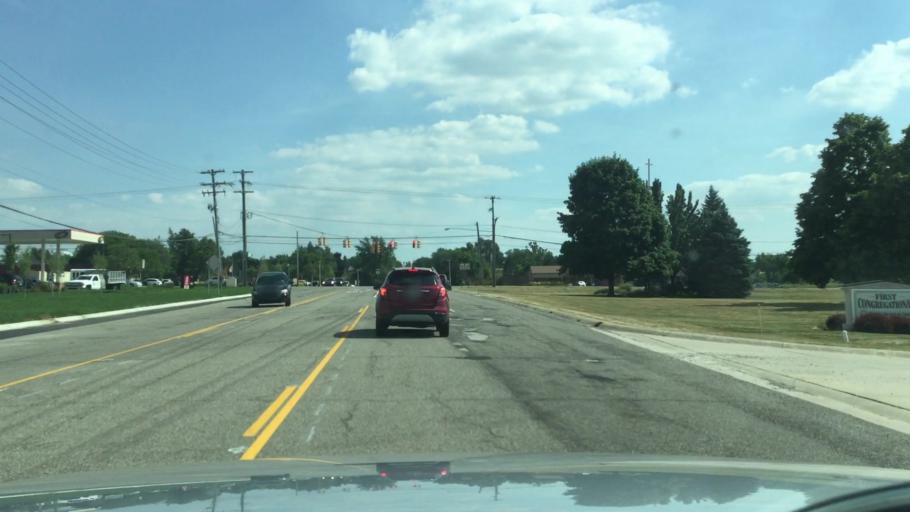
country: US
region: Michigan
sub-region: Genesee County
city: Grand Blanc
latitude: 42.9322
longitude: -83.5969
